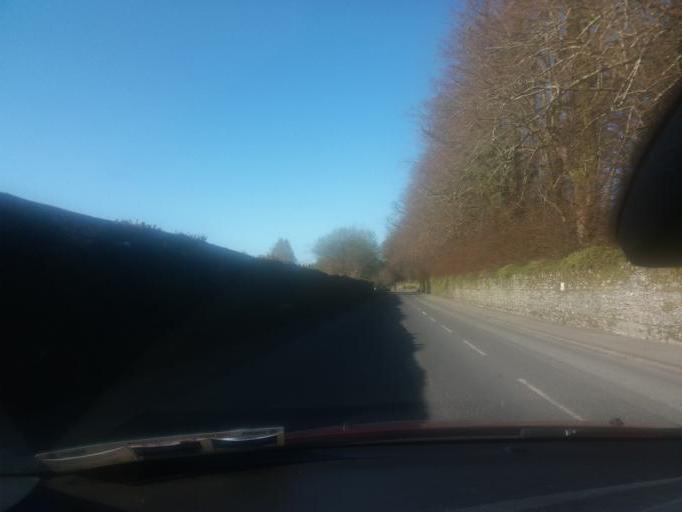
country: IE
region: Munster
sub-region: Ciarrai
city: Cill Airne
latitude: 52.0489
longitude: -9.5190
